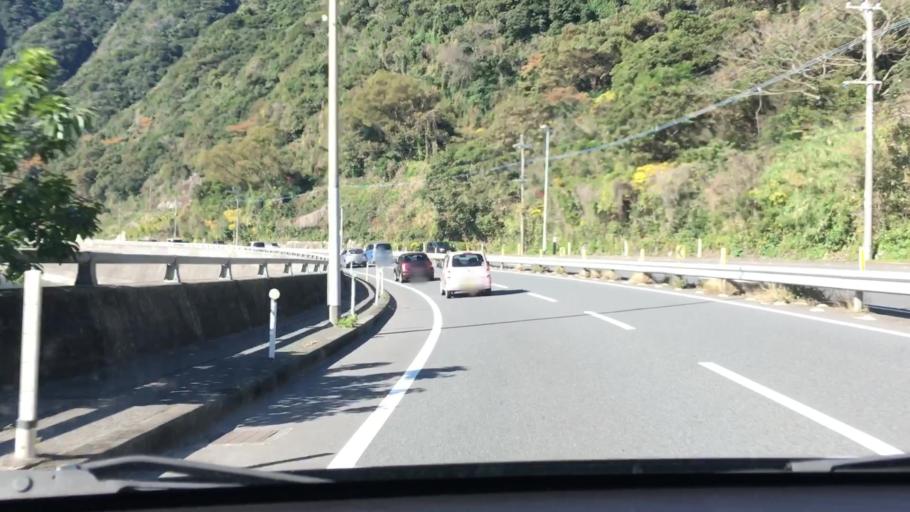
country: JP
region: Kagoshima
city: Kajiki
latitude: 31.6565
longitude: 130.6151
